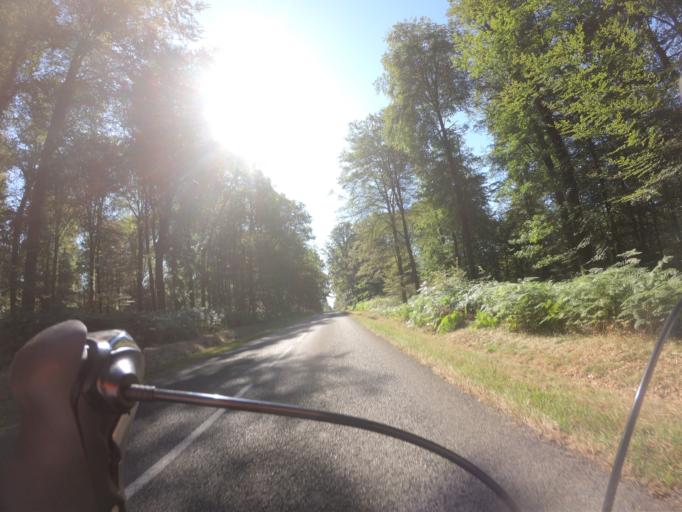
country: FR
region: Lower Normandy
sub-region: Departement de l'Orne
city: Tesse-la-Madeleine
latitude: 48.5736
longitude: -0.4560
